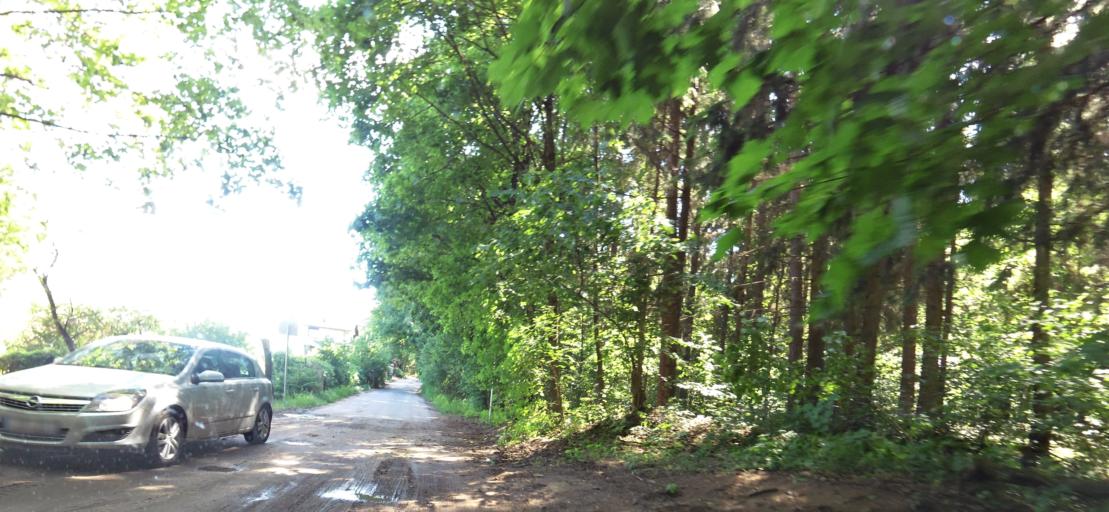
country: LT
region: Vilnius County
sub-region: Vilnius
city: Fabijoniskes
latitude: 54.8260
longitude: 25.3199
